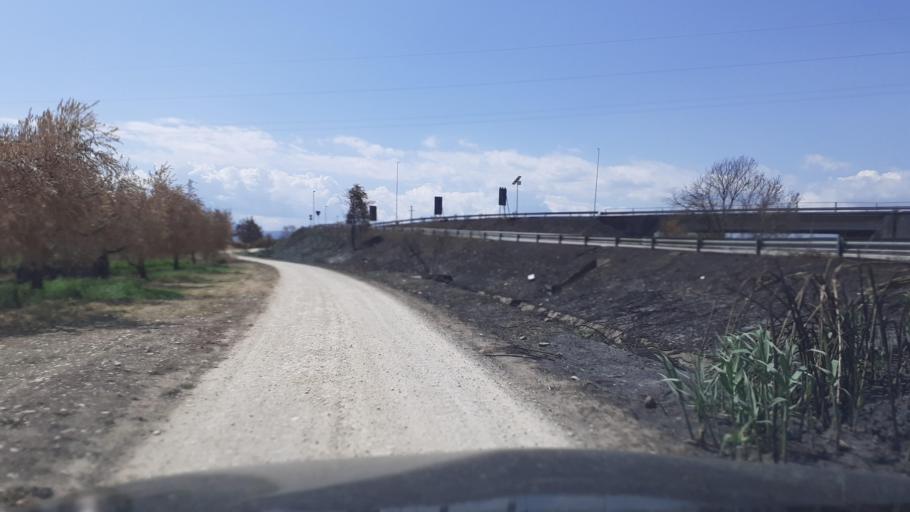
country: IT
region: Abruzzo
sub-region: Provincia di Chieti
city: Fossacesia
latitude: 42.2161
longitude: 14.4969
